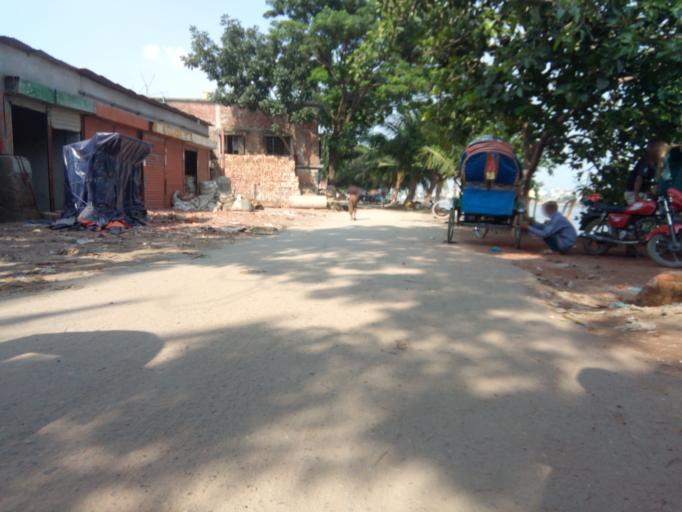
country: BD
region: Dhaka
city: Azimpur
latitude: 23.7088
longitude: 90.3820
